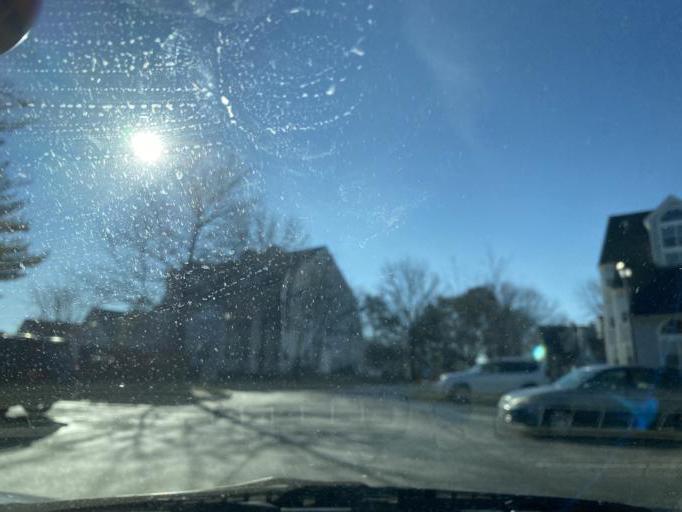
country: US
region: Maryland
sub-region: Prince George's County
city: Laurel
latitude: 39.0862
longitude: -76.8677
